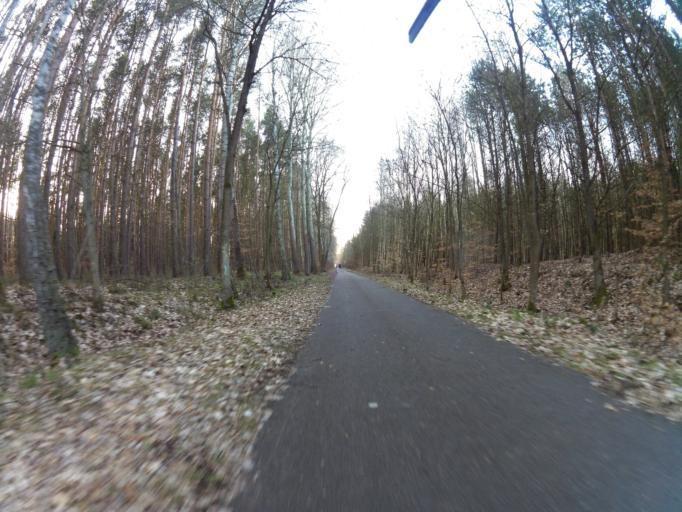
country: PL
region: West Pomeranian Voivodeship
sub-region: Powiat policki
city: Nowe Warpno
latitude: 53.7144
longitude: 14.3139
